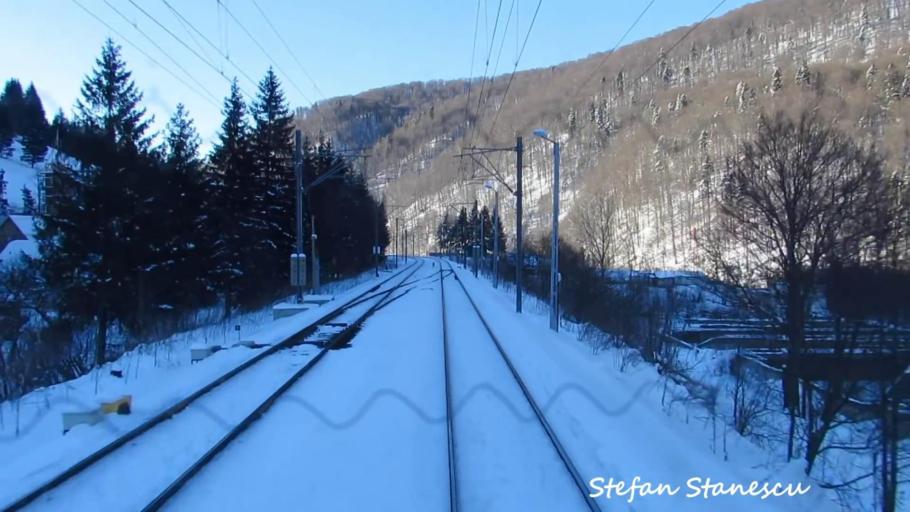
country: RO
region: Prahova
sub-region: Oras Azuga
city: Azuga
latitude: 45.4328
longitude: 25.5523
